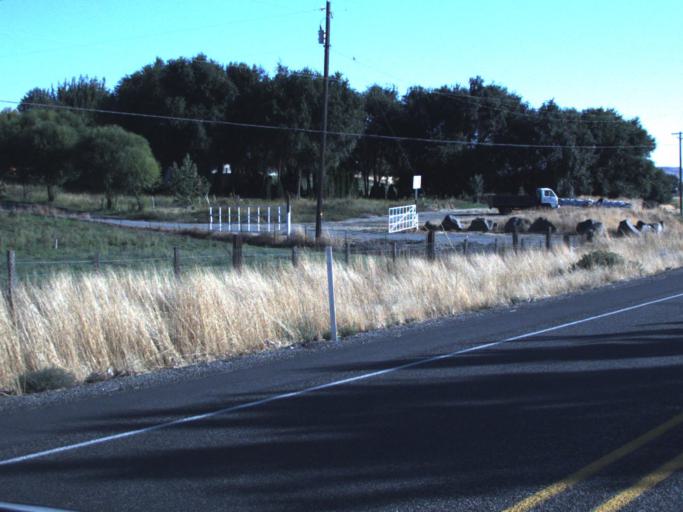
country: US
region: Washington
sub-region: Benton County
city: Finley
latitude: 46.1885
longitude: -119.0755
